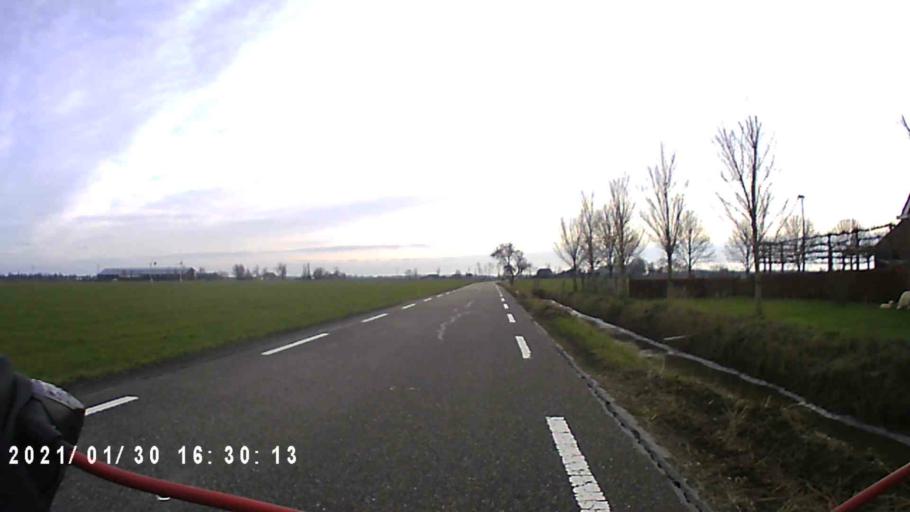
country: NL
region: Groningen
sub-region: Gemeente Zuidhorn
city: Zuidhorn
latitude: 53.2205
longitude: 6.3871
